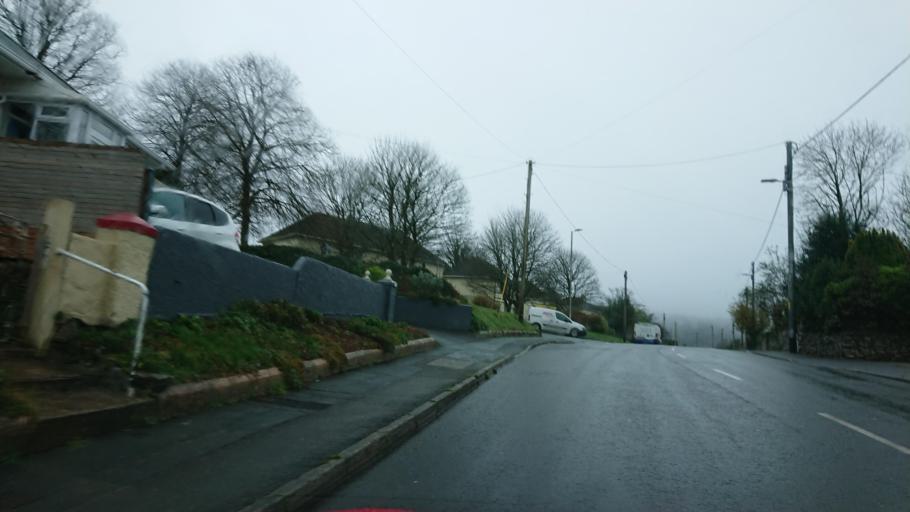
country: GB
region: England
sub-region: Plymouth
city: Plymstock
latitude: 50.3567
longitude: -4.0992
